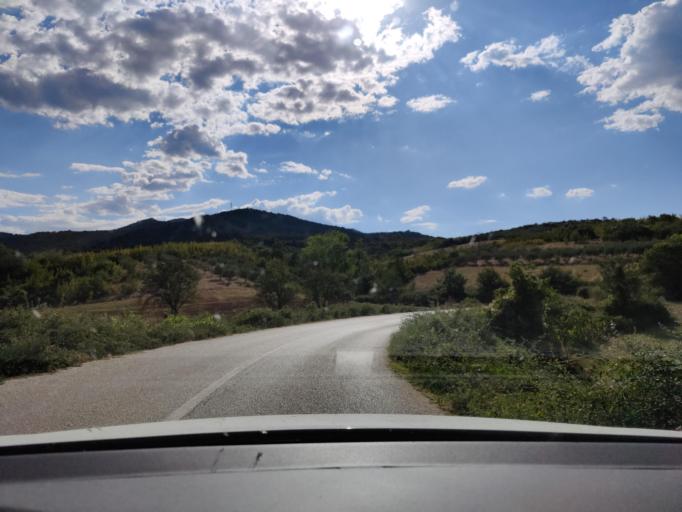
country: GR
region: Central Macedonia
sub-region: Nomos Serron
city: Chrysochorafa
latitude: 41.1424
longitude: 23.2148
